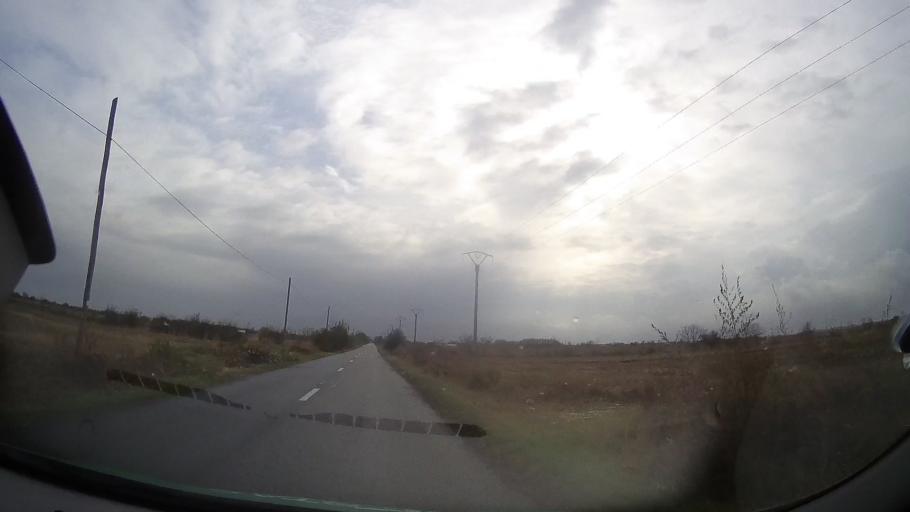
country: RO
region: Ialomita
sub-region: Comuna Fierbinti-Targ
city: Fierbintii de Jos
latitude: 44.7069
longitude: 26.3922
